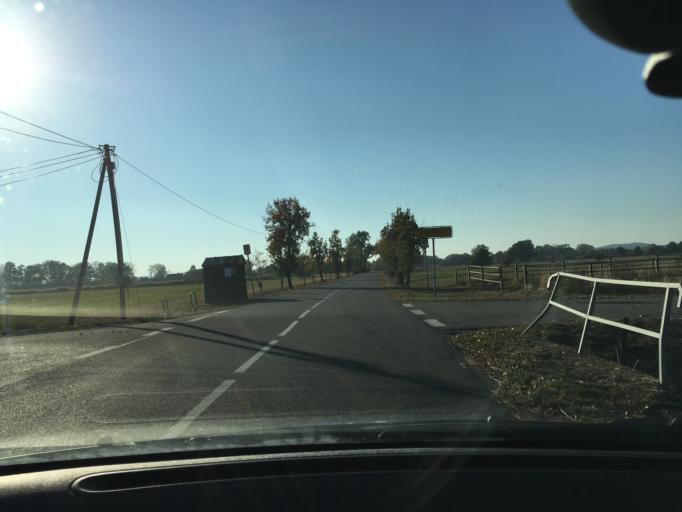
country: DE
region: Lower Saxony
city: Dannenberg
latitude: 53.1507
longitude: 11.1022
